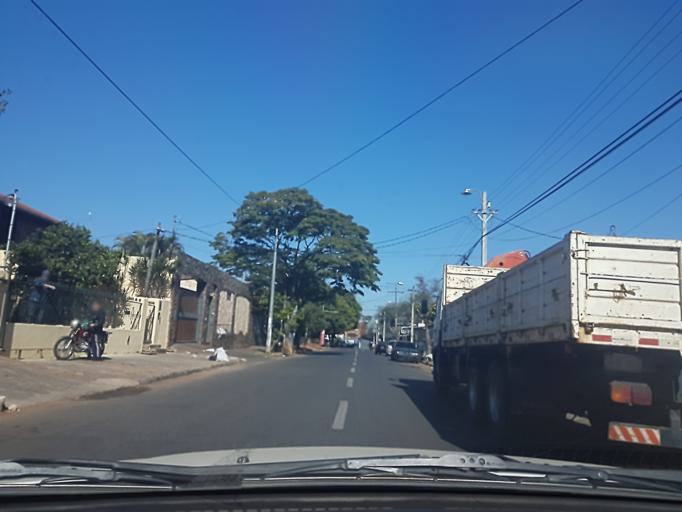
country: PY
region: Central
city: Lambare
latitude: -25.3198
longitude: -57.6033
